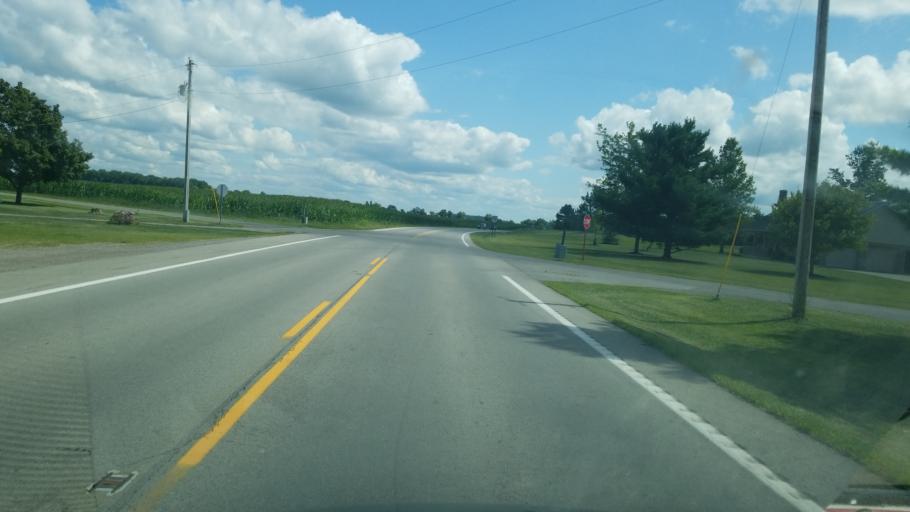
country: US
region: Ohio
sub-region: Putnam County
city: Kalida
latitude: 40.9478
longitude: -84.1633
